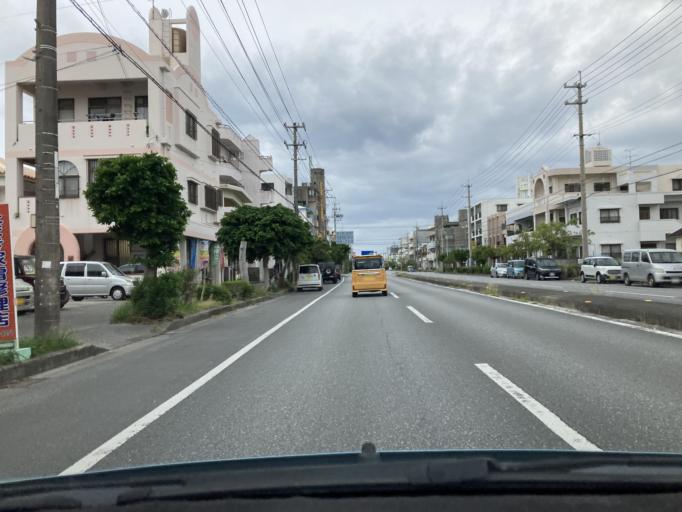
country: JP
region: Okinawa
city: Itoman
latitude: 26.1409
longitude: 127.6675
